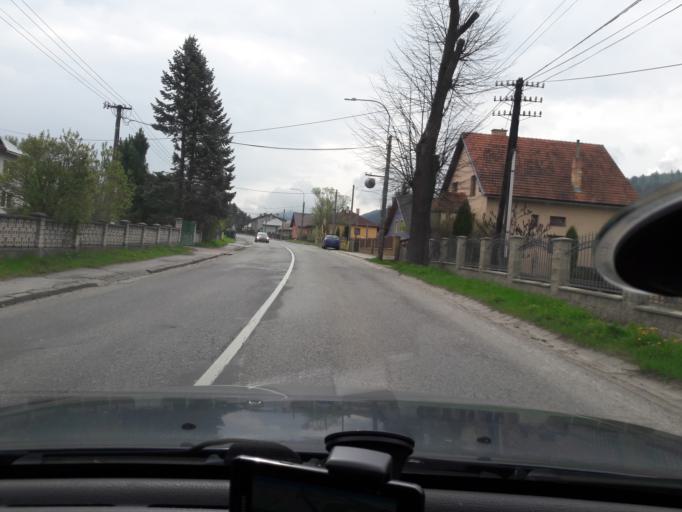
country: SK
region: Banskobystricky
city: Cierny Balog
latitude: 48.7640
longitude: 19.7747
